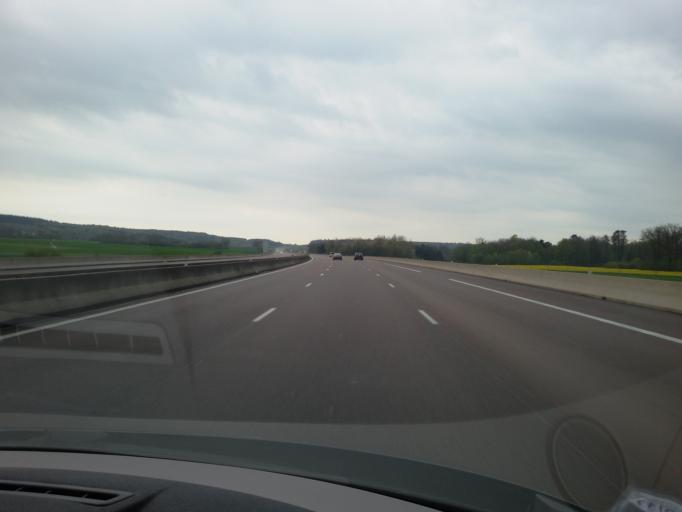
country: FR
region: Champagne-Ardenne
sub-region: Departement de la Haute-Marne
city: Langres
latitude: 47.8462
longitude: 5.2317
